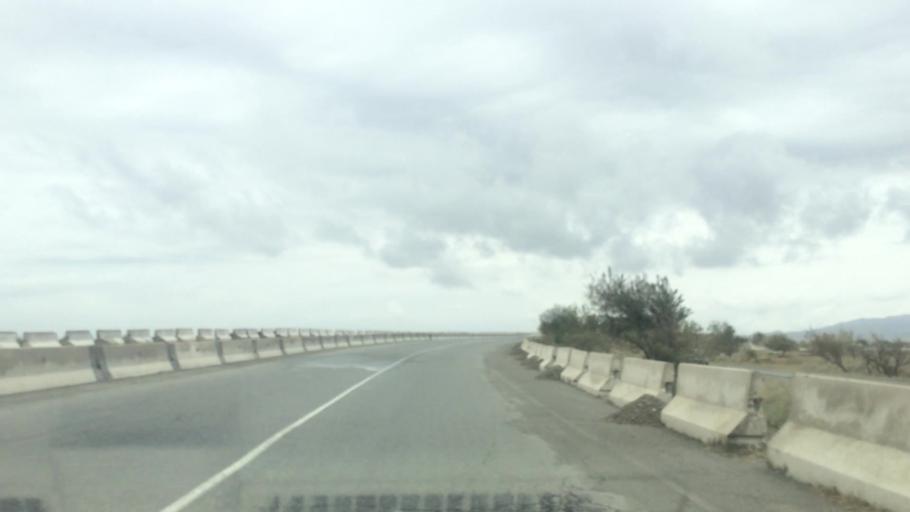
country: UZ
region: Samarqand
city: Bulung'ur
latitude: 39.8365
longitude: 67.4423
